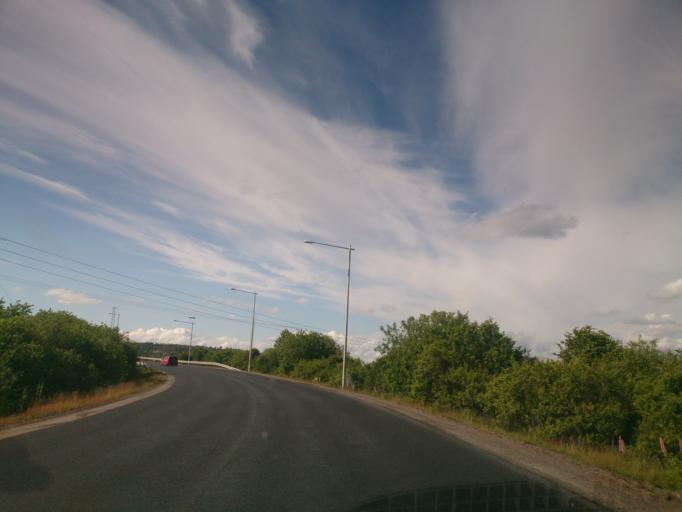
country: SE
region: OEstergoetland
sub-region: Norrkopings Kommun
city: Jursla
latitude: 58.6412
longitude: 16.1671
